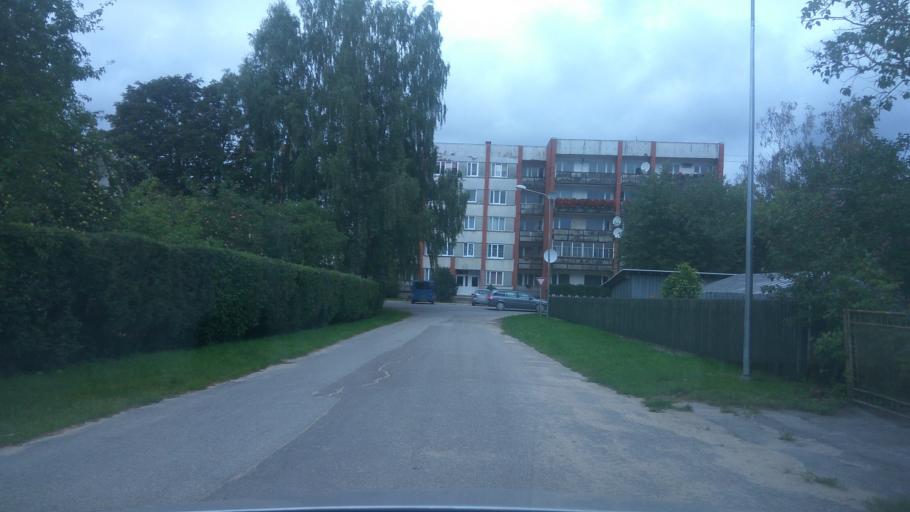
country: LV
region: Kuldigas Rajons
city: Kuldiga
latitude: 56.9725
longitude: 21.9535
